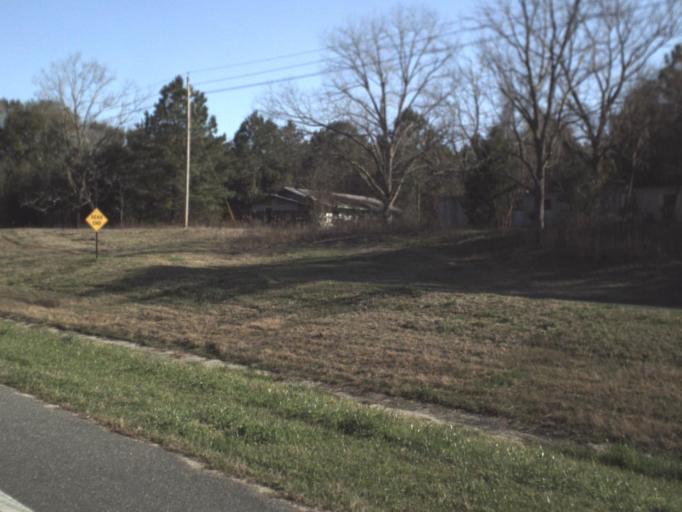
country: US
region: Florida
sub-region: Jackson County
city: Marianna
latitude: 30.7882
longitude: -85.3551
